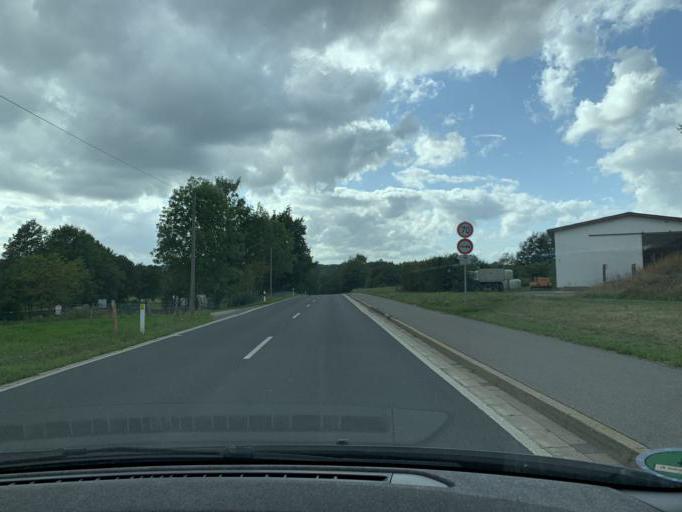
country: DE
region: North Rhine-Westphalia
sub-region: Regierungsbezirk Koln
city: Simmerath
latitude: 50.6280
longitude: 6.3067
